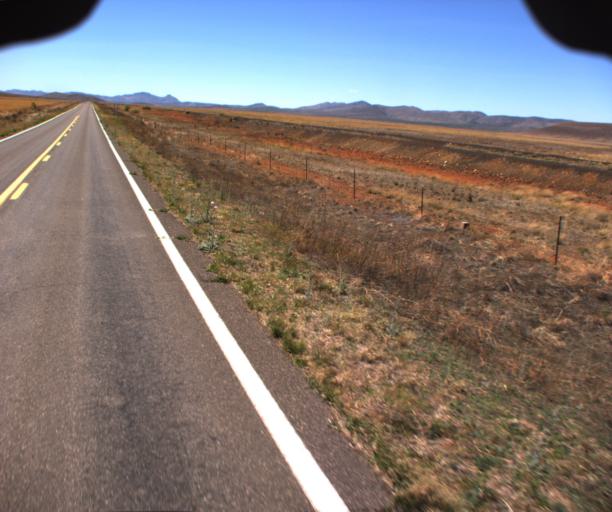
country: US
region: Arizona
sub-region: Cochise County
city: Douglas
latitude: 31.6084
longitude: -109.2234
